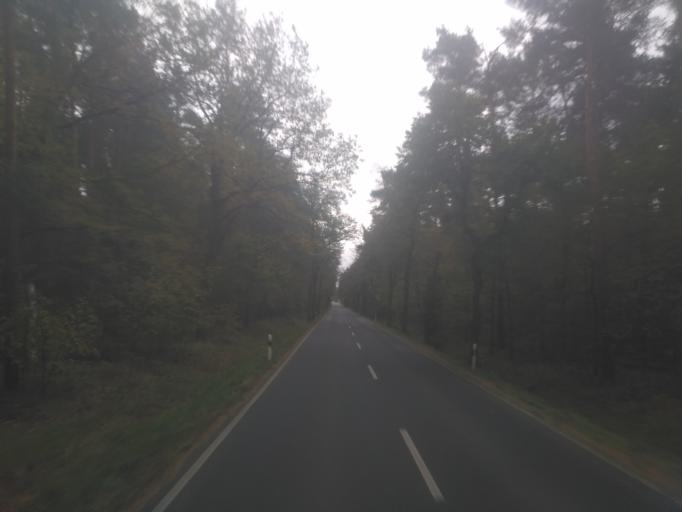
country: DE
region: Brandenburg
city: Merzdorf
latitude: 51.3921
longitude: 13.5071
